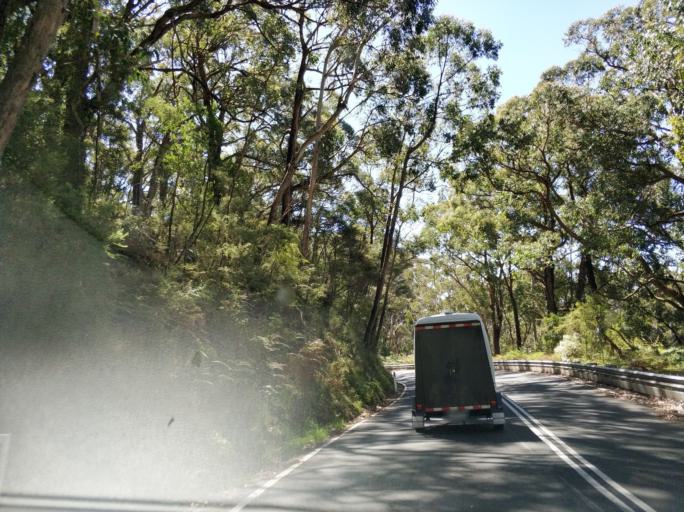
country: AU
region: Victoria
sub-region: Colac-Otway
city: Apollo Bay
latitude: -38.7449
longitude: 143.2571
